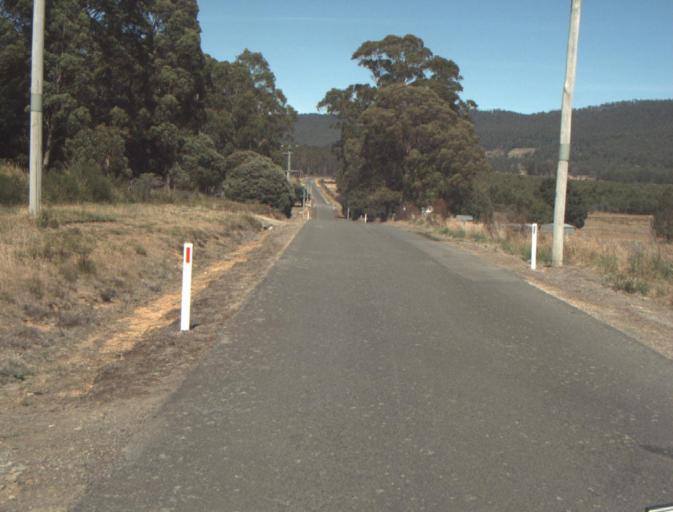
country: AU
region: Tasmania
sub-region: Launceston
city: Newstead
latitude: -41.3199
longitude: 147.3239
